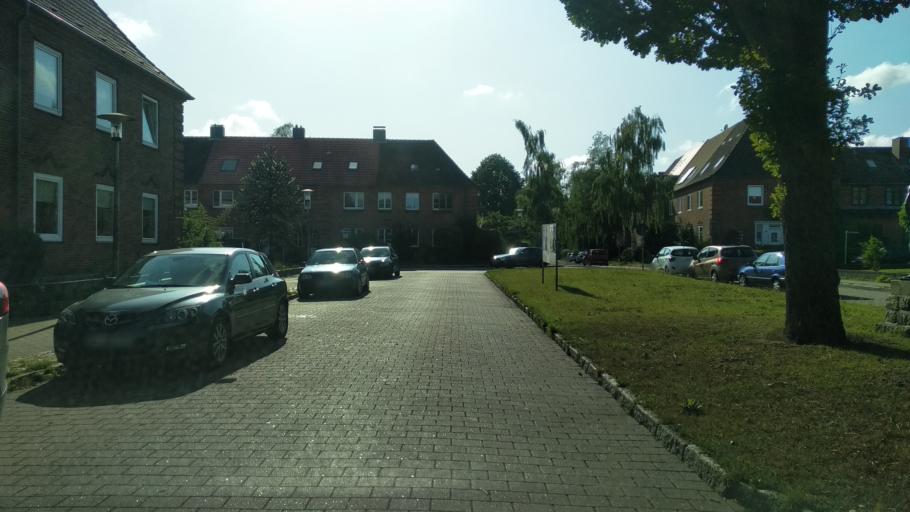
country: DE
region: Schleswig-Holstein
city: Schleswig
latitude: 54.5180
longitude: 9.5541
